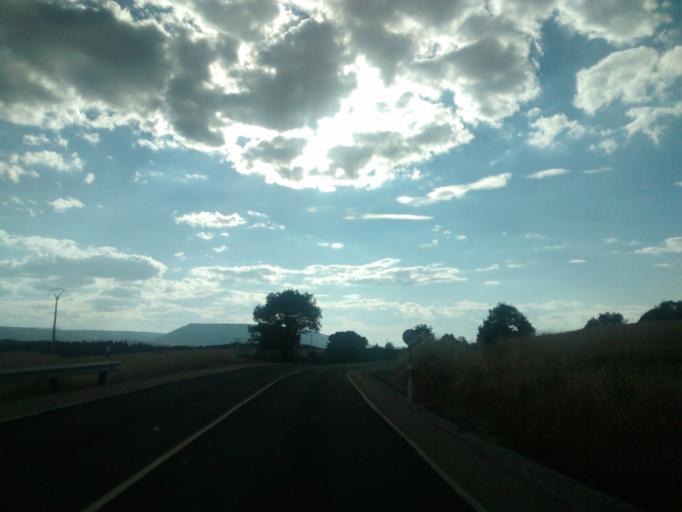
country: ES
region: Castille and Leon
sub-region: Provincia de Burgos
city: Basconcillos del Tozo
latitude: 42.6853
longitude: -3.9687
